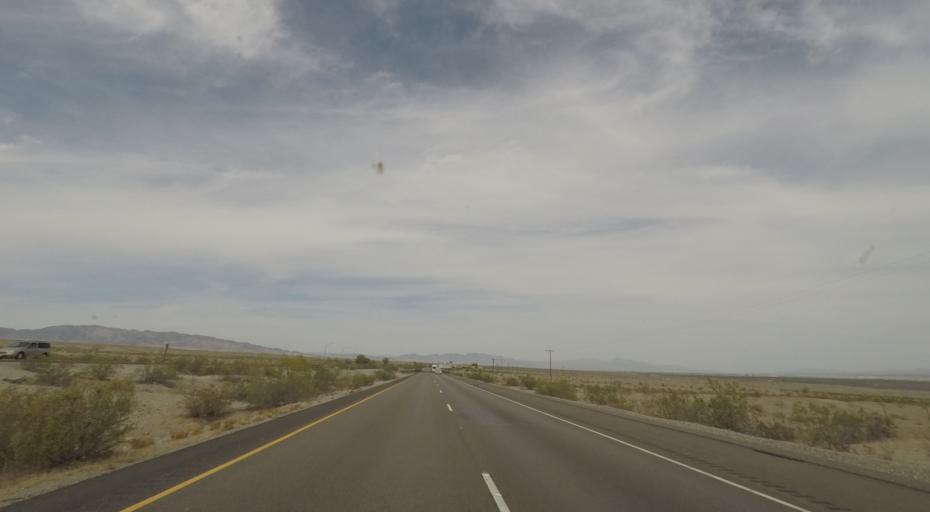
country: US
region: California
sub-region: San Bernardino County
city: Needles
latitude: 34.7477
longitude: -114.5615
